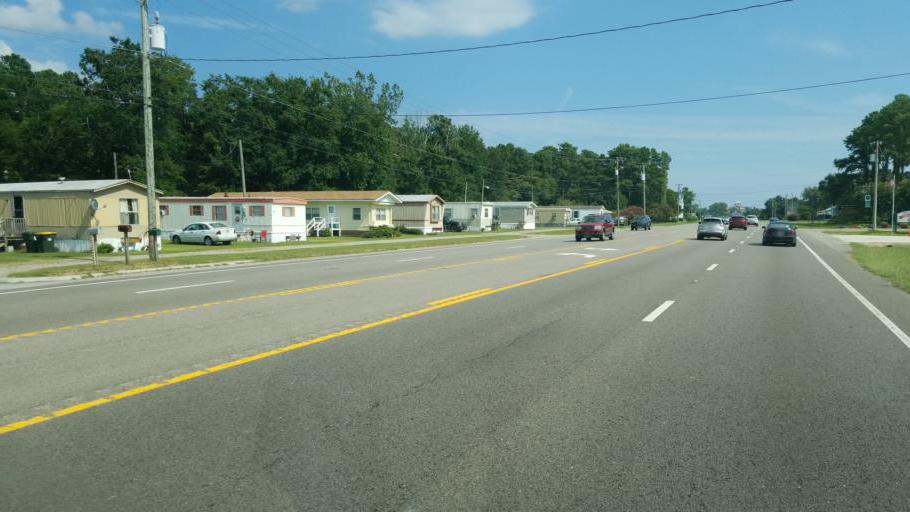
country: US
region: North Carolina
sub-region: Dare County
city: Southern Shores
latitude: 36.1230
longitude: -75.8345
